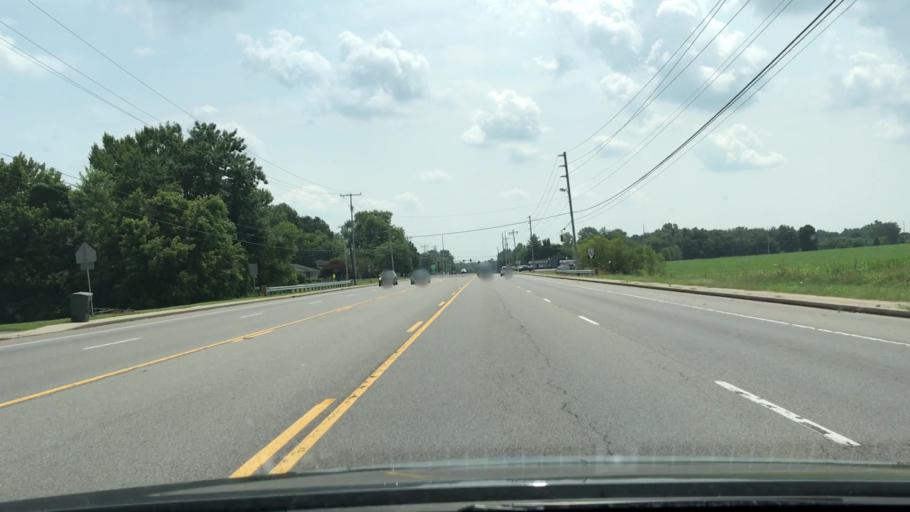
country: US
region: Tennessee
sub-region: Sumner County
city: Portland
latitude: 36.5529
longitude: -86.5074
